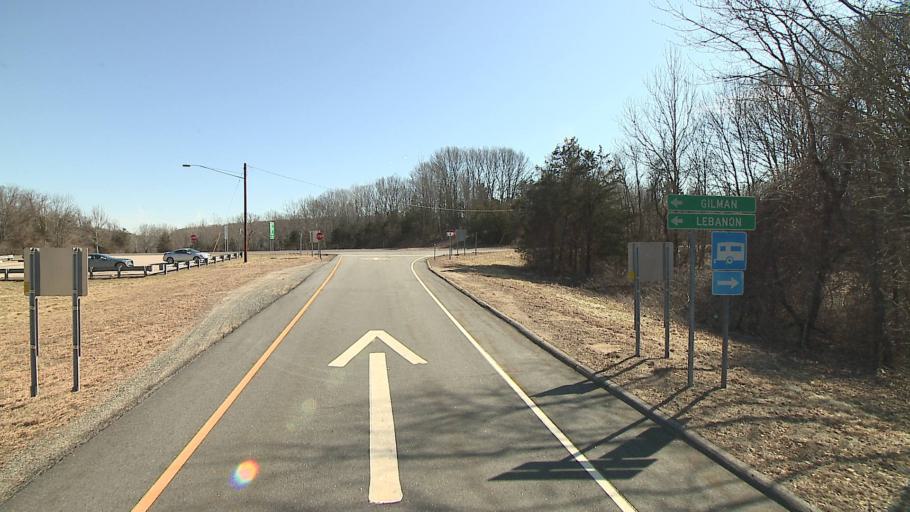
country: US
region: Connecticut
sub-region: New London County
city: Montville Center
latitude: 41.5691
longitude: -72.2095
